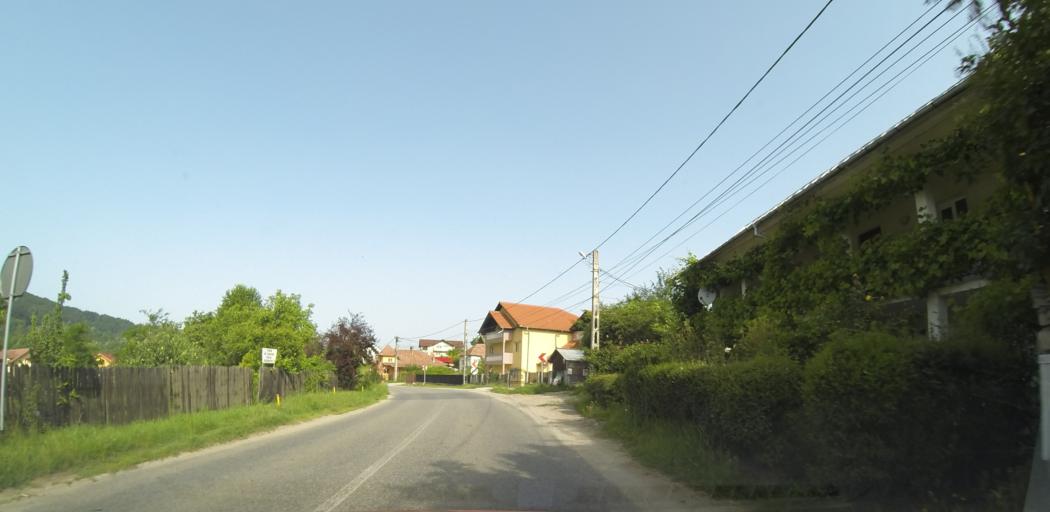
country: RO
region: Valcea
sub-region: Comuna Vladesti
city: Vladesti
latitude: 45.1261
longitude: 24.2807
